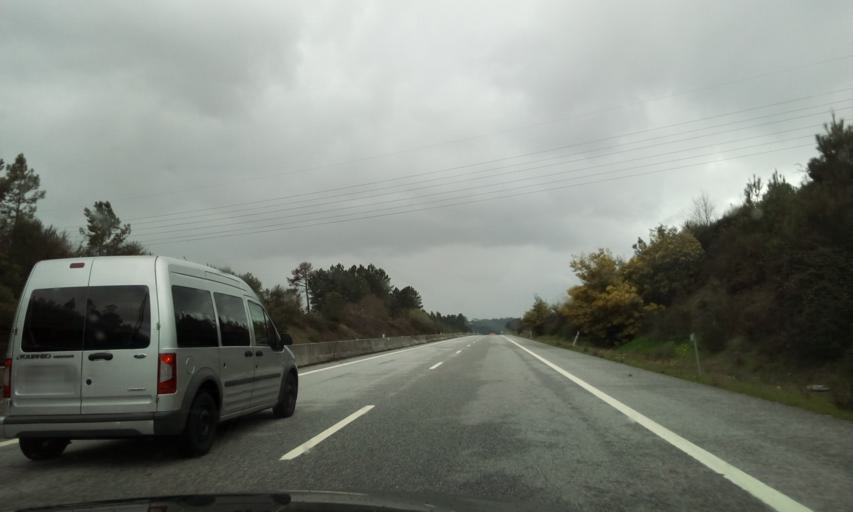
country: PT
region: Viseu
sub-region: Viseu
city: Rio de Loba
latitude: 40.6416
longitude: -7.8739
